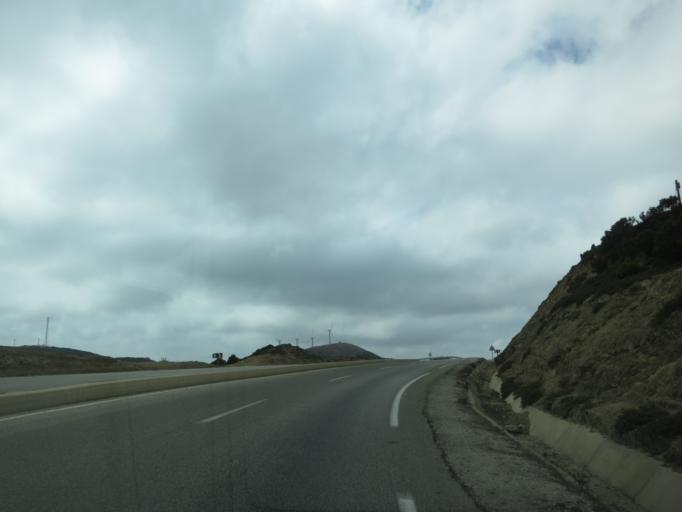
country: ES
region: Ceuta
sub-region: Ceuta
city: Ceuta
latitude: 35.8589
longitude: -5.4296
